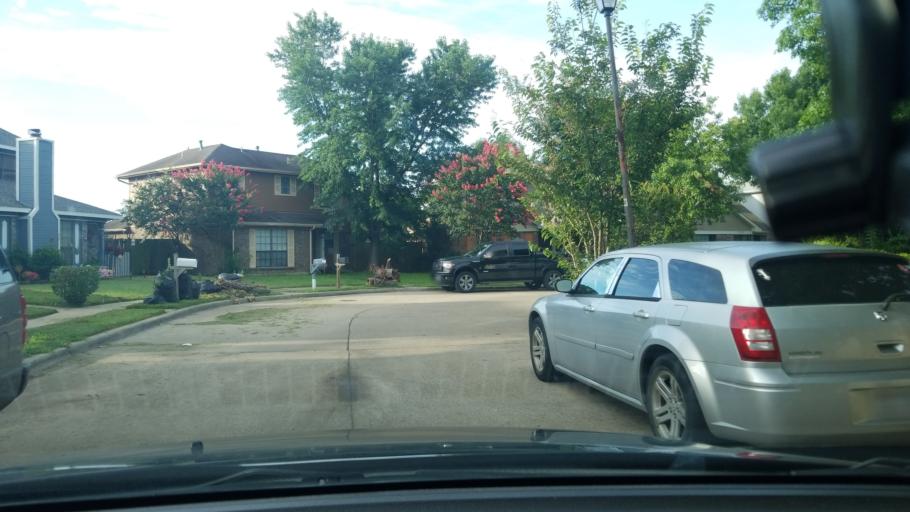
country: US
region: Texas
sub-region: Dallas County
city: Balch Springs
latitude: 32.7583
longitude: -96.6442
